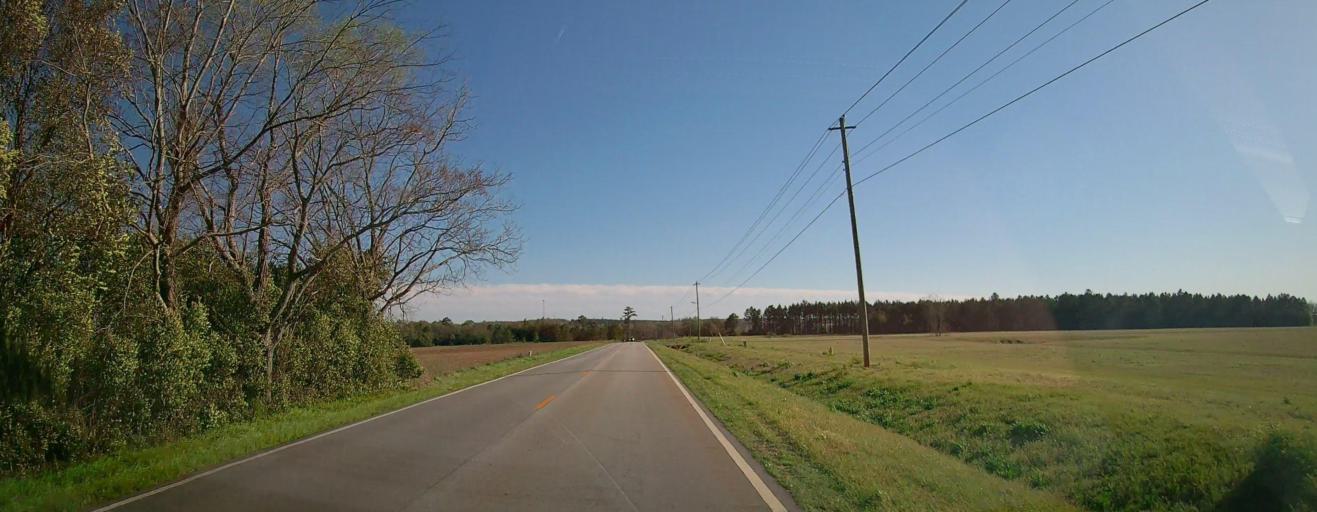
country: US
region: Georgia
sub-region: Houston County
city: Perry
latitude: 32.4352
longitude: -83.7367
